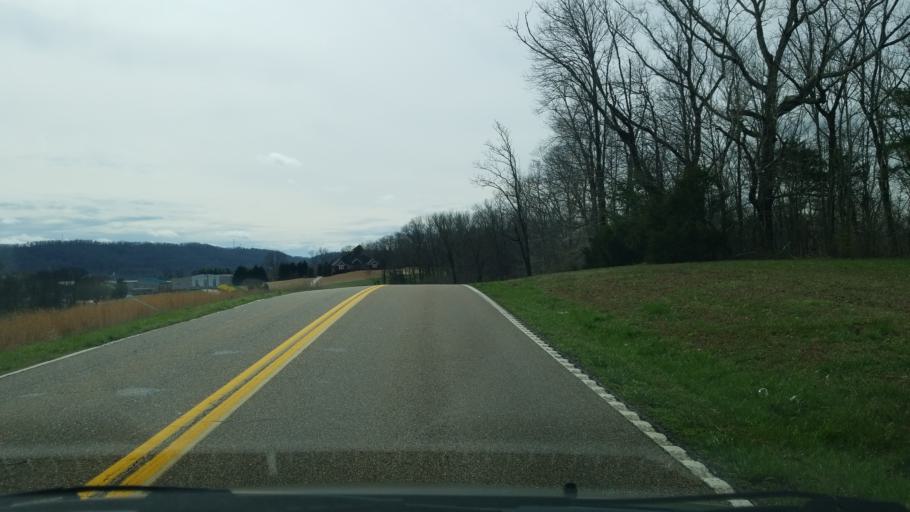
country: US
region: Tennessee
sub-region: Hamilton County
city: Collegedale
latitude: 35.0993
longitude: -85.0646
